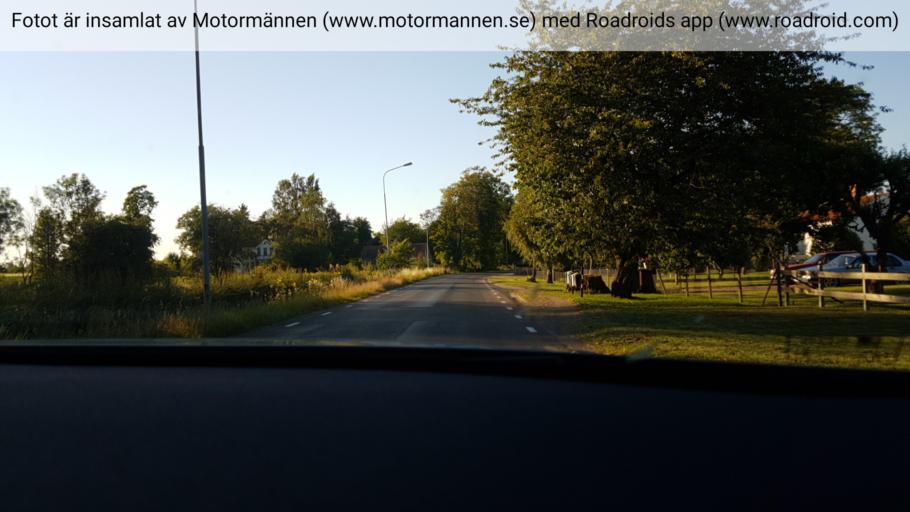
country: SE
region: Vaestra Goetaland
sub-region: Skovde Kommun
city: Skultorp
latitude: 58.2506
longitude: 13.7845
